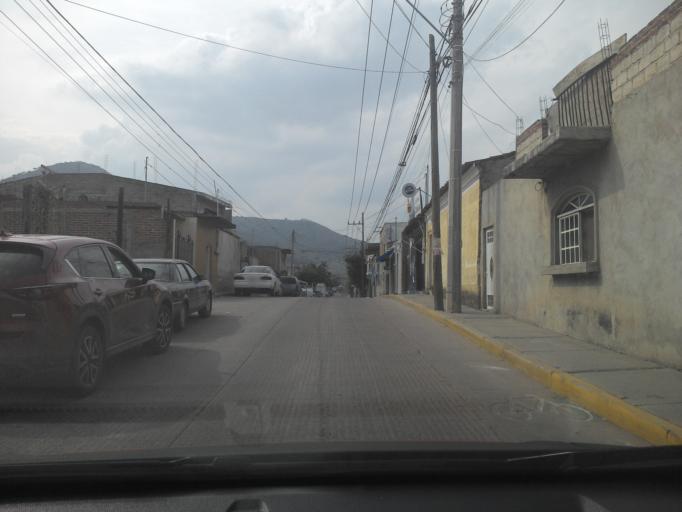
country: MX
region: Jalisco
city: Tlajomulco de Zuniga
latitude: 20.4772
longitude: -103.4450
